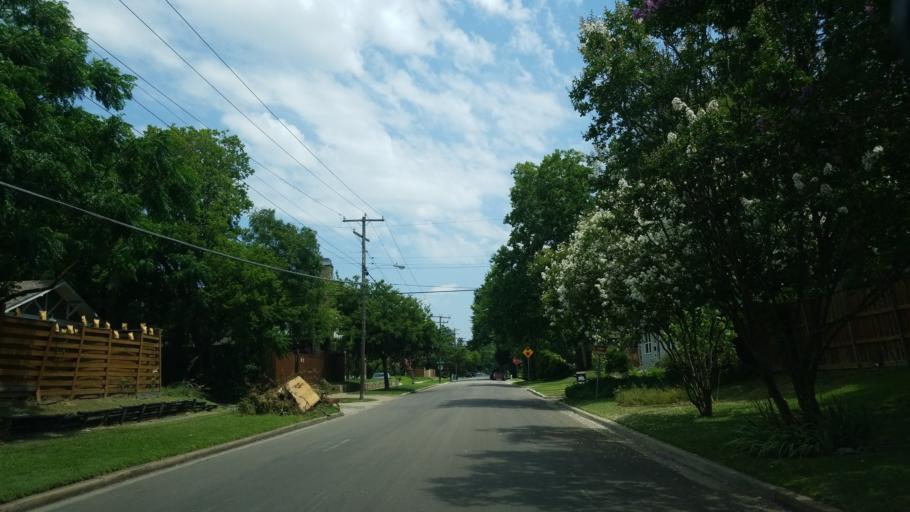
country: US
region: Texas
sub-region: Dallas County
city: Highland Park
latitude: 32.8189
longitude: -96.7659
